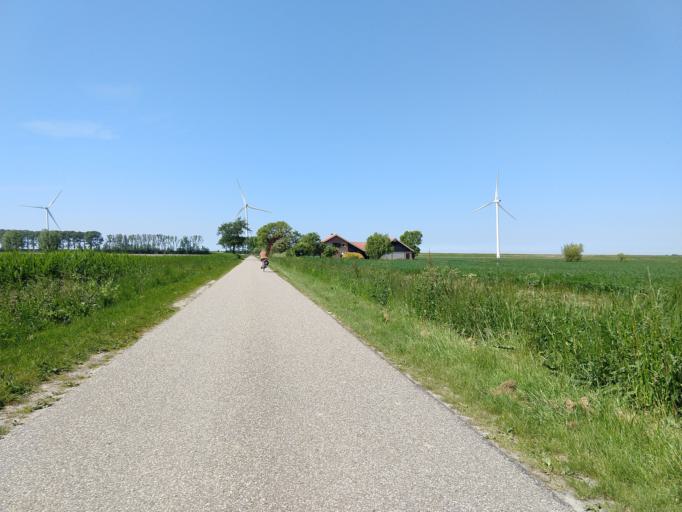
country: NL
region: Zeeland
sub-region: Schouwen-Duiveland
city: Bruinisse
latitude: 51.6035
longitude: 4.0678
